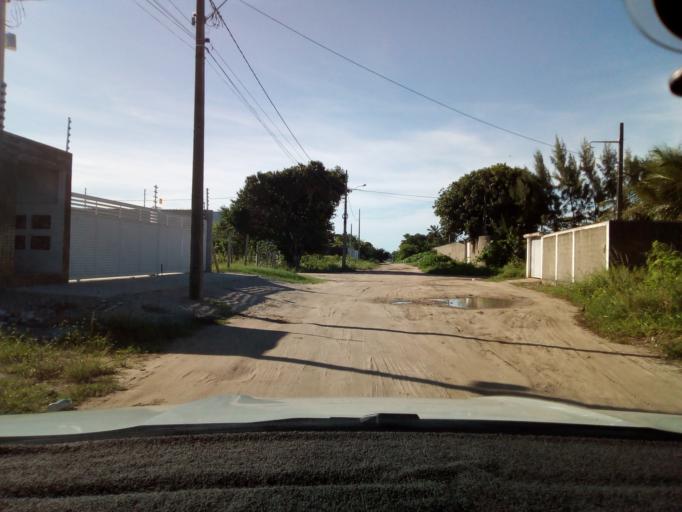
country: BR
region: Paraiba
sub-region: Joao Pessoa
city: Joao Pessoa
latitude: -7.1516
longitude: -34.8153
